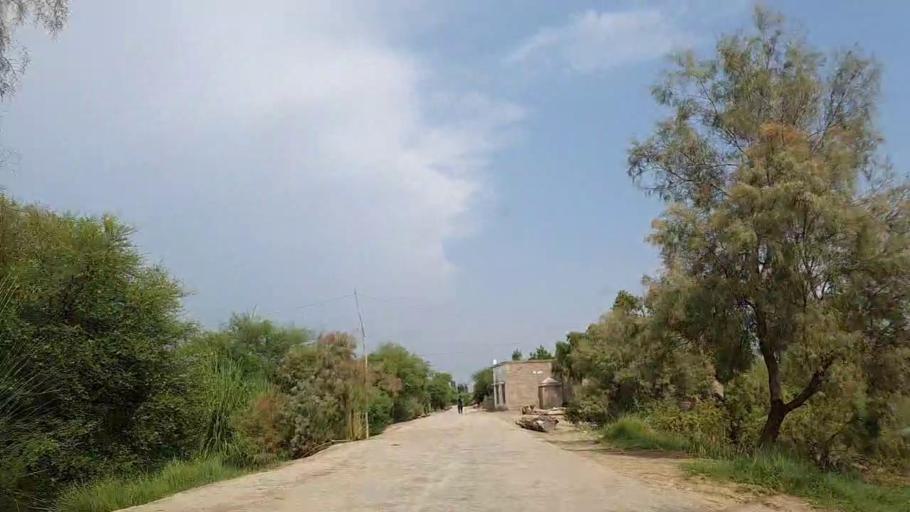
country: PK
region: Sindh
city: Khanpur
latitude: 27.8391
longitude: 69.4799
